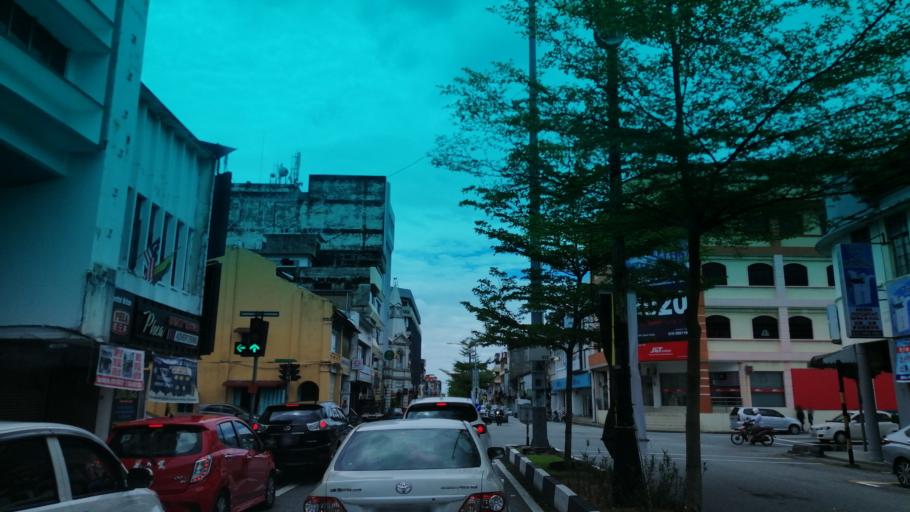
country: MY
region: Perak
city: Taiping
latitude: 4.8527
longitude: 100.7426
